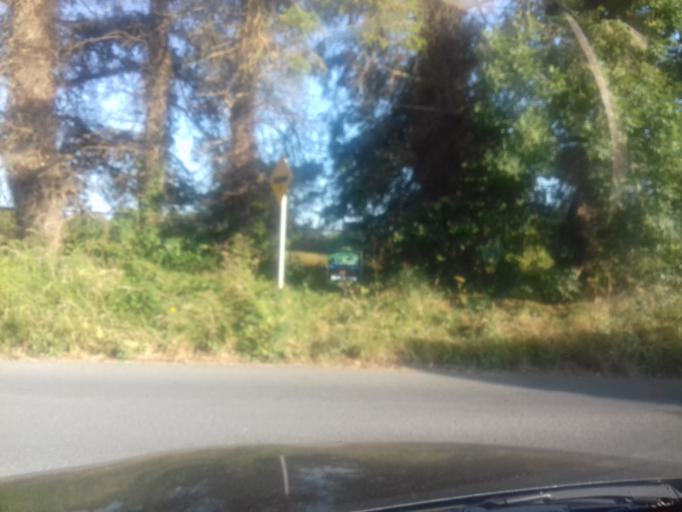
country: IE
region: Leinster
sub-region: Fingal County
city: Blanchardstown
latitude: 53.4312
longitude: -6.3751
